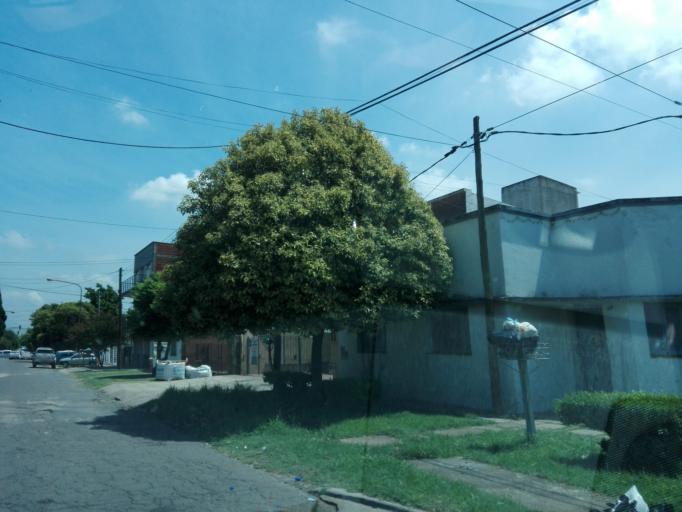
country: AR
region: Buenos Aires
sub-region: Partido de La Plata
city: La Plata
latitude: -34.9419
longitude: -57.9874
